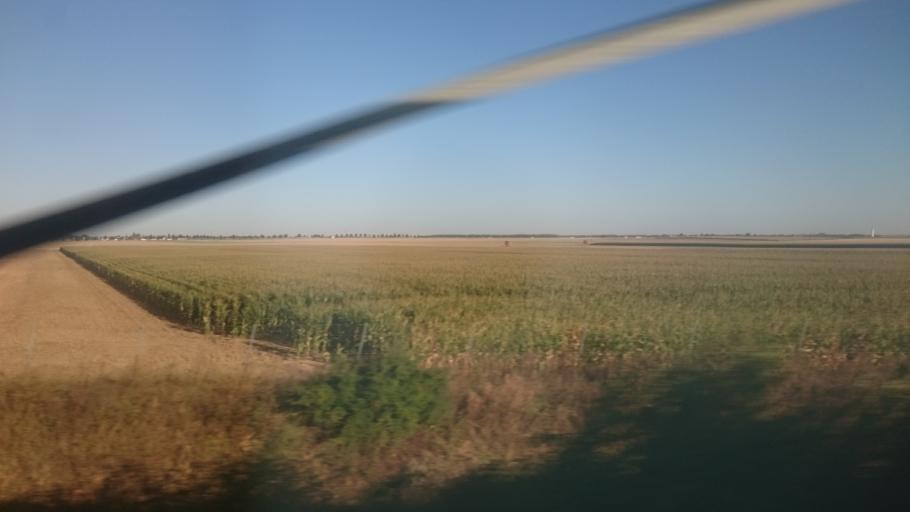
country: FR
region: Centre
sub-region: Departement d'Eure-et-Loir
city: Bonneval
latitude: 48.2110
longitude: 1.4191
